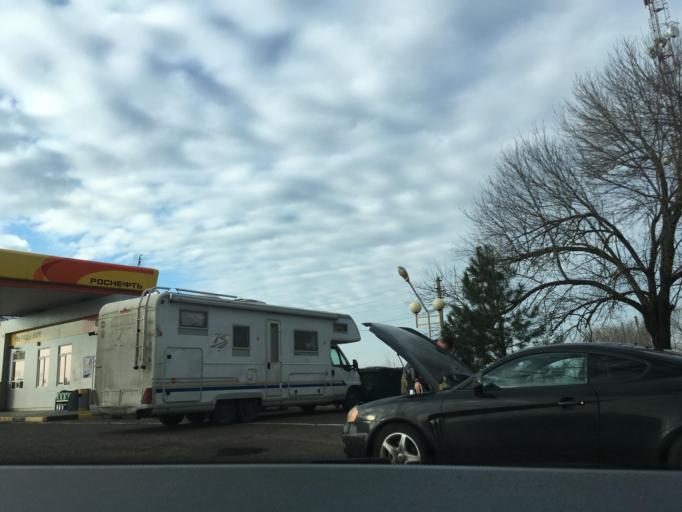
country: RU
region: Krasnodarskiy
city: Irkliyevskaya
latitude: 45.8413
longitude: 39.6781
